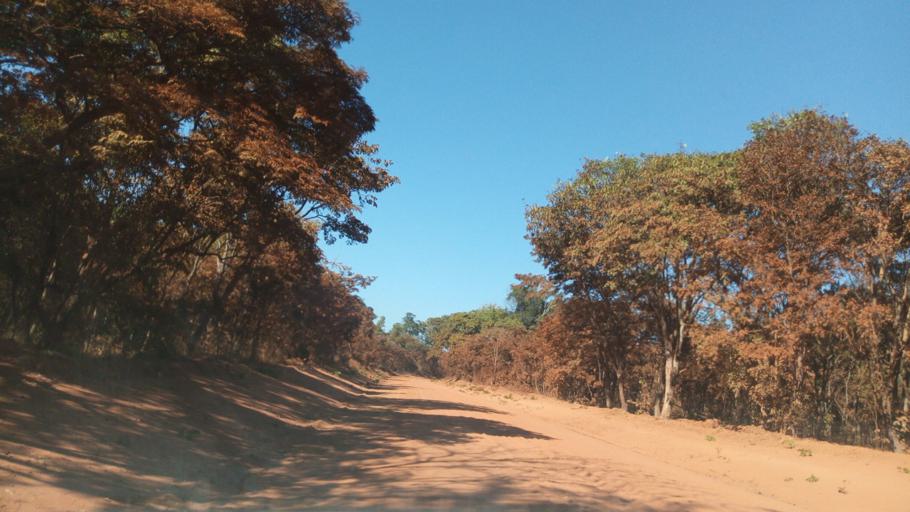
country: ZM
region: Luapula
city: Mwense
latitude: -10.7472
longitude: 28.3260
